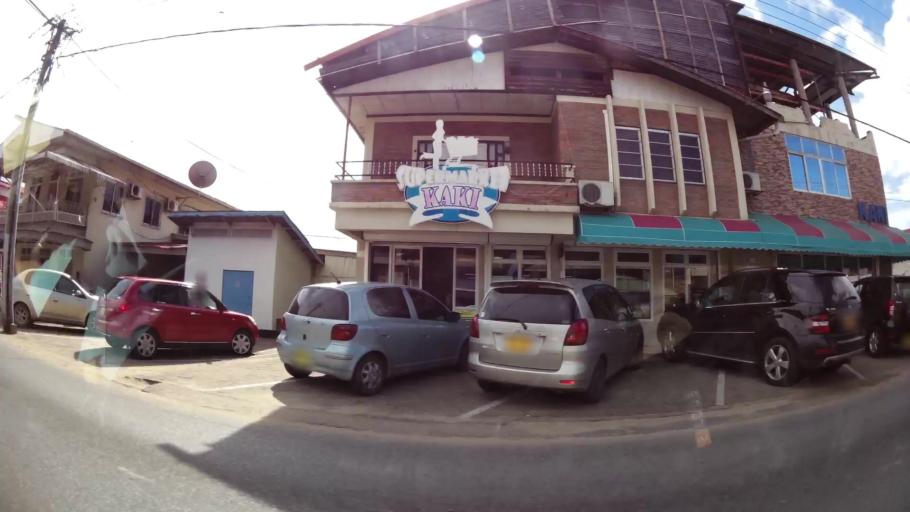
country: SR
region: Paramaribo
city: Paramaribo
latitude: 5.8424
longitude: -55.1497
